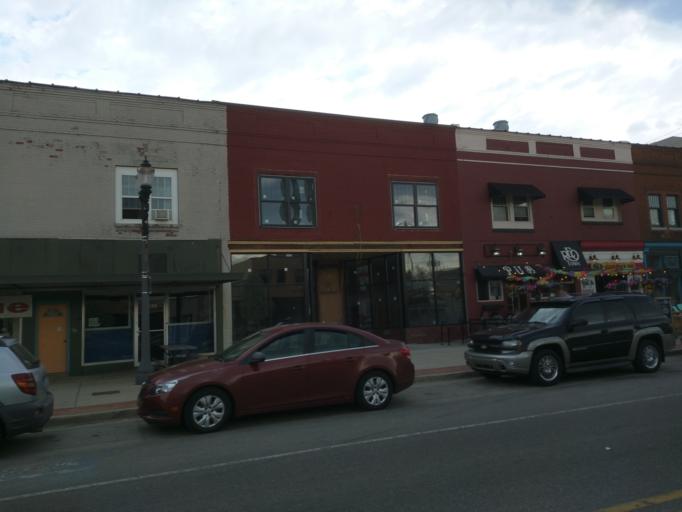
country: US
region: Michigan
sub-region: Ingham County
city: Lansing
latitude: 42.7206
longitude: -84.5524
